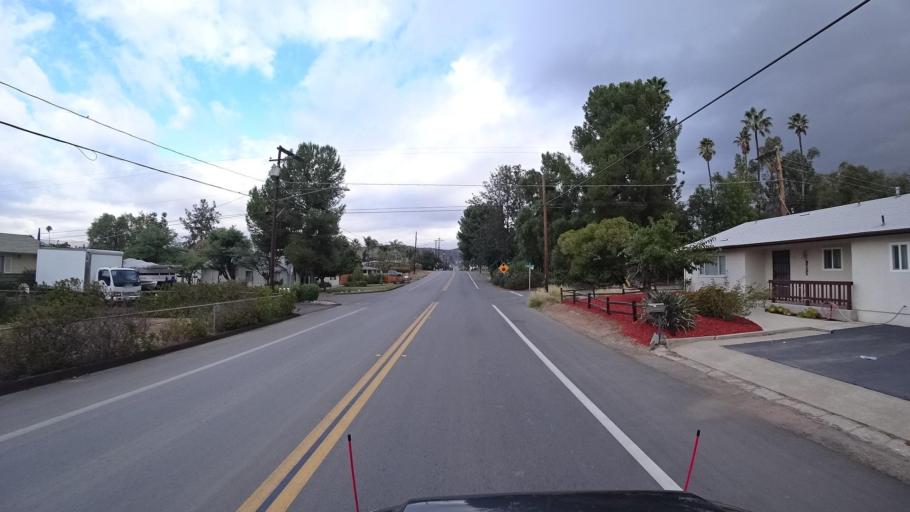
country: US
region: California
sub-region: San Diego County
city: Lakeside
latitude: 32.8577
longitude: -116.9085
